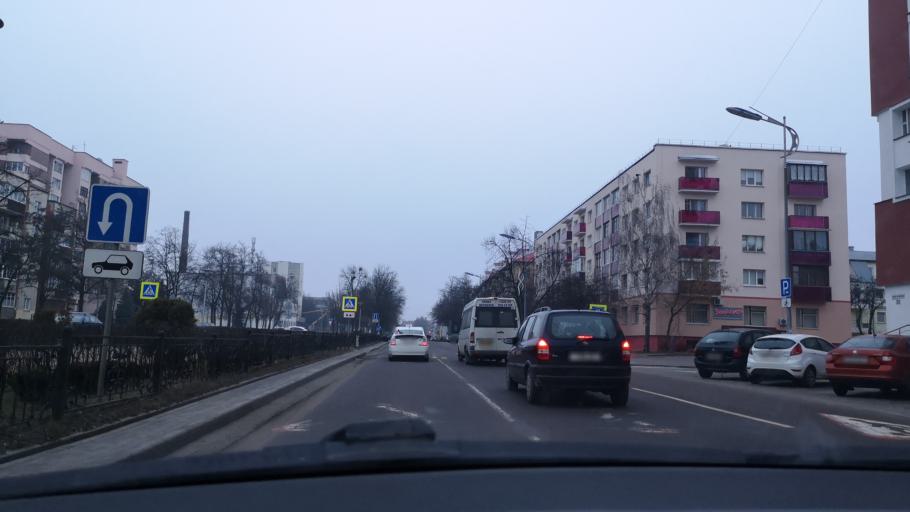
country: BY
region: Brest
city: Brest
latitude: 52.0891
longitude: 23.7022
